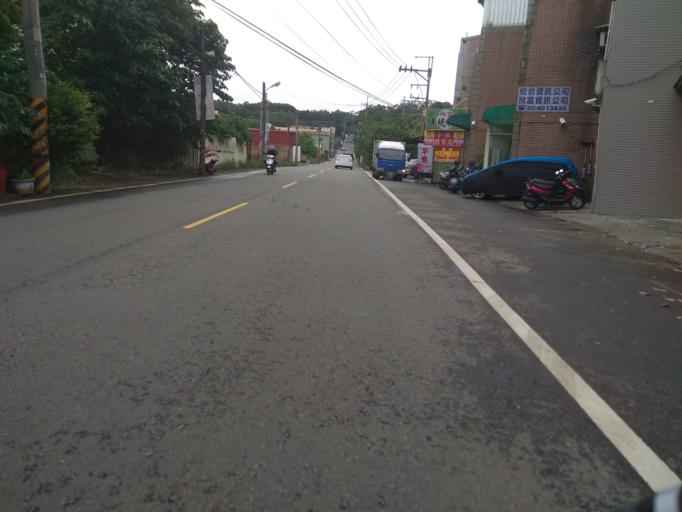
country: TW
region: Taiwan
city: Daxi
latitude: 24.9423
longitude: 121.1886
